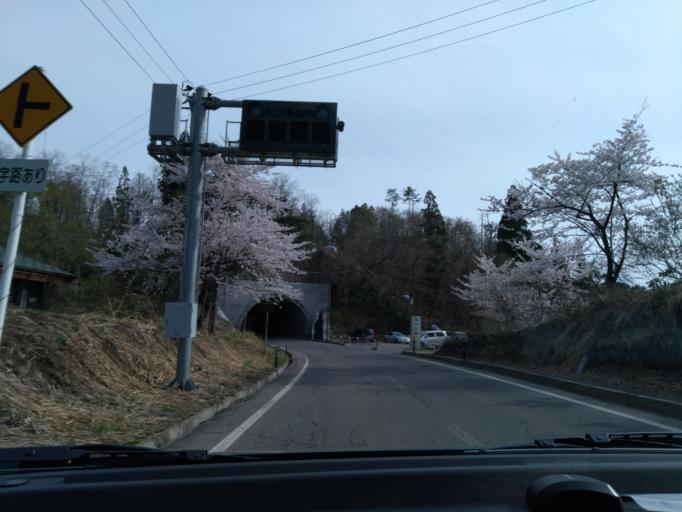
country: JP
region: Akita
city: Yokotemachi
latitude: 39.3240
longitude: 140.5734
